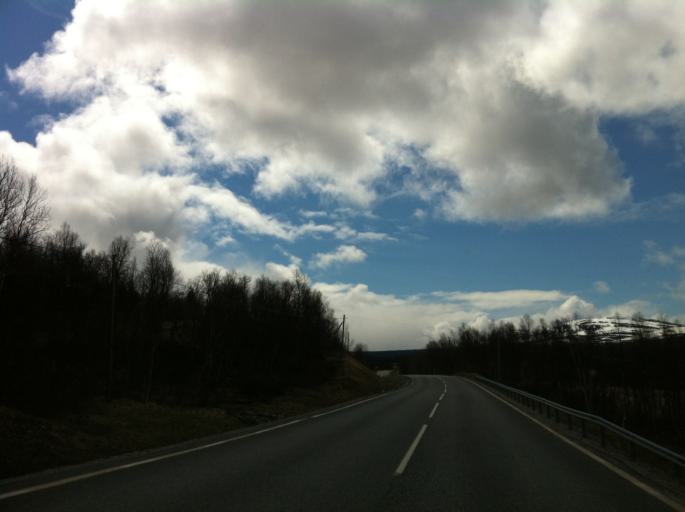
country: NO
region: Sor-Trondelag
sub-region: Tydal
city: Aas
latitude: 62.6679
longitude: 12.4297
